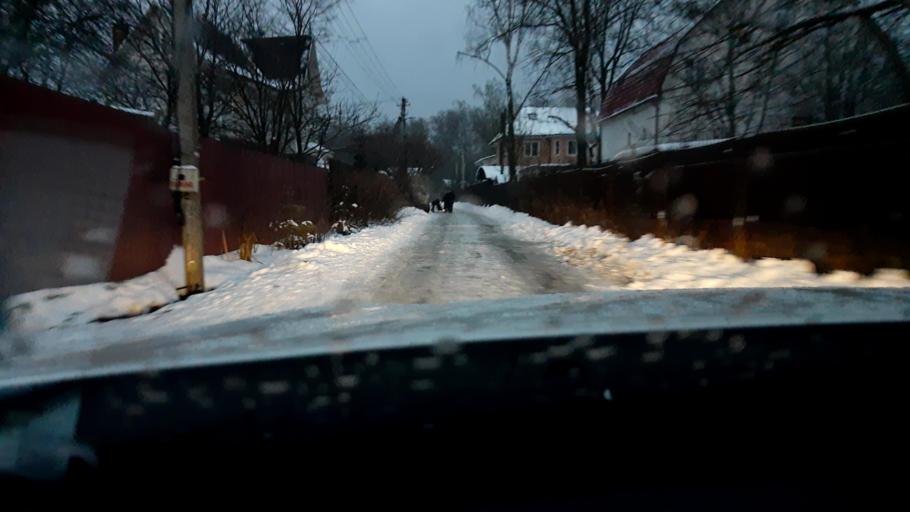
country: RU
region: Moskovskaya
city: Kommunarka
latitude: 55.5921
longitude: 37.4877
